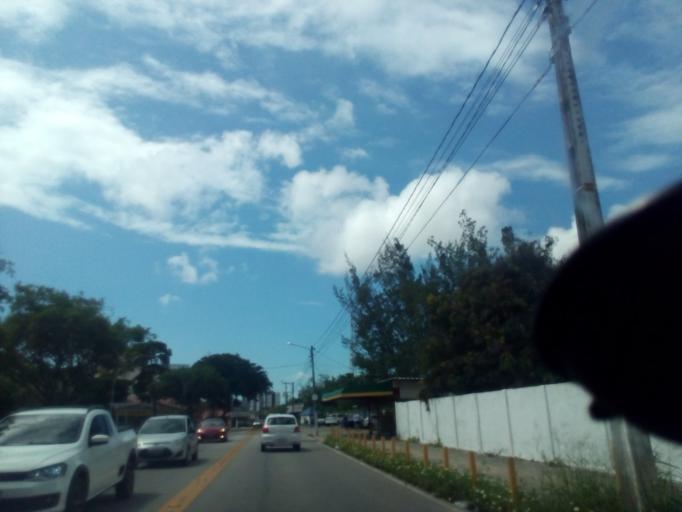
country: BR
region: Rio Grande do Norte
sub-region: Natal
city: Natal
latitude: -5.8381
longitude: -35.2181
